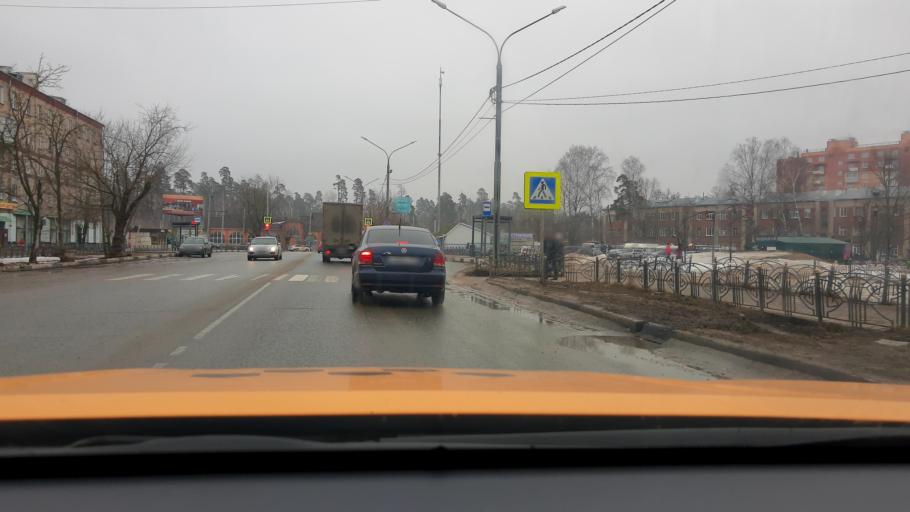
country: RU
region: Moskovskaya
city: Noginsk
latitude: 55.8838
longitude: 38.4490
